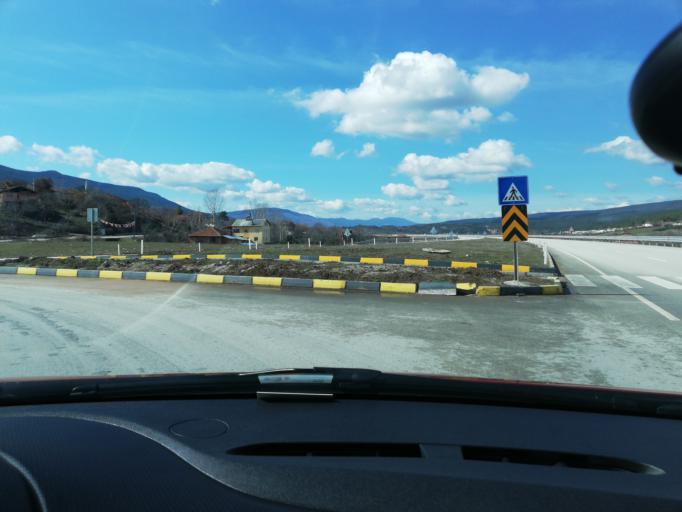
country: TR
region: Kastamonu
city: Igdir
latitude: 41.2299
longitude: 33.0164
